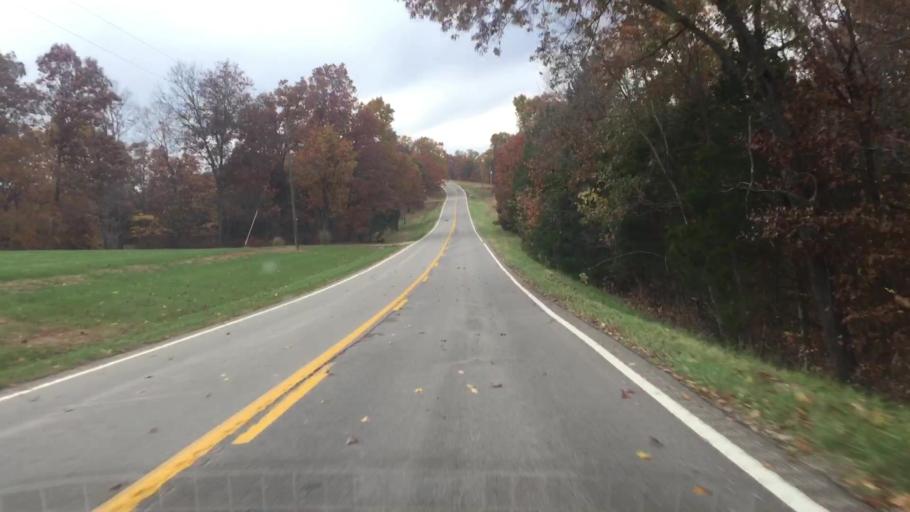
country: US
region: Missouri
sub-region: Gasconade County
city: Hermann
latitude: 38.7108
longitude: -91.6344
